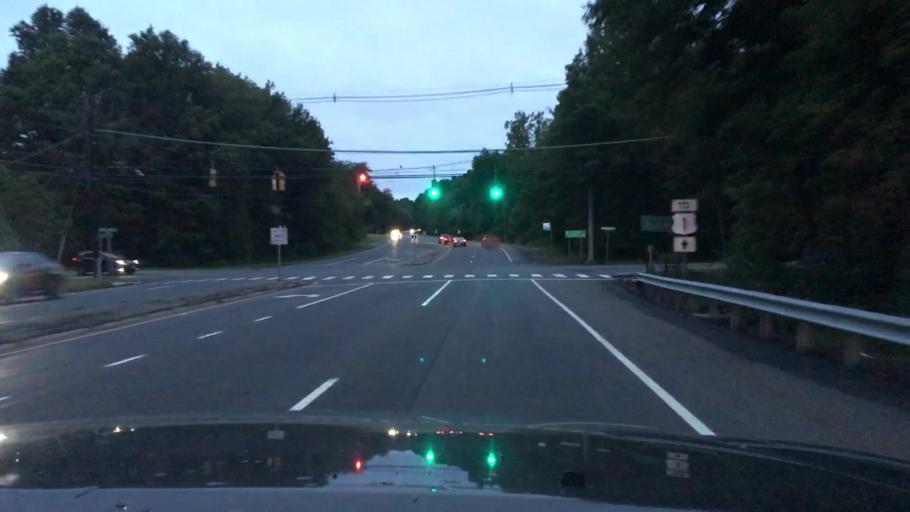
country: US
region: Connecticut
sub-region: Fairfield County
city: Westport
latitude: 41.1264
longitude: -73.3324
